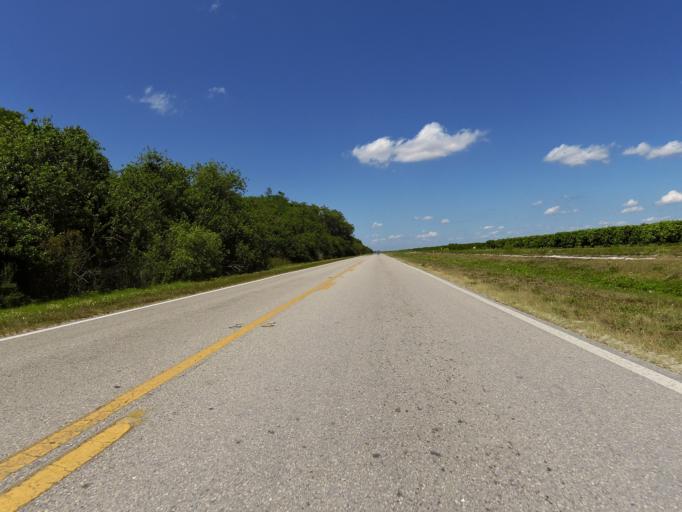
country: US
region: Florida
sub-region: Collier County
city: Immokalee
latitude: 26.2972
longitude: -81.4159
